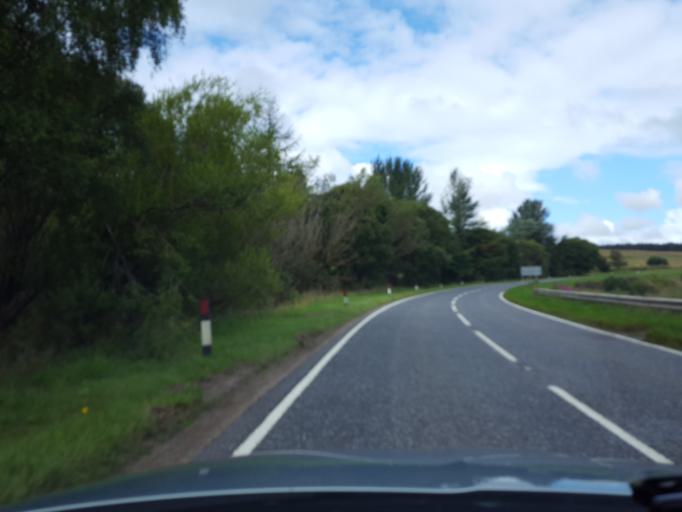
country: GB
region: Scotland
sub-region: Moray
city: Rothes
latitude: 57.5351
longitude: -3.2211
